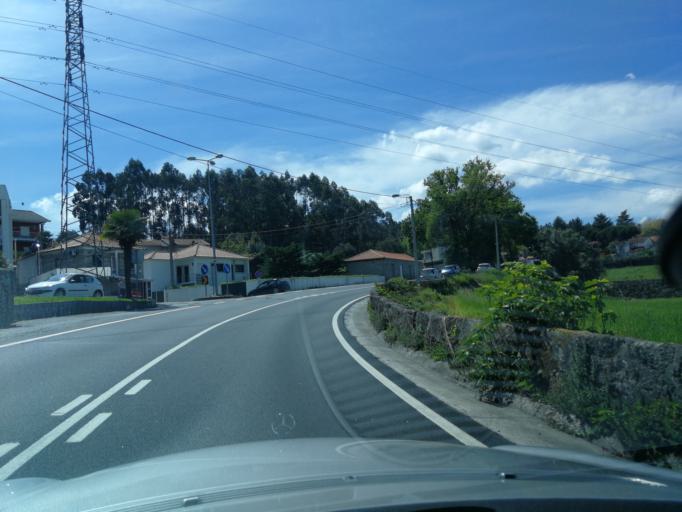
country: PT
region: Braga
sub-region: Vila Nova de Famalicao
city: Calendario
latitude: 41.4234
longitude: -8.5342
